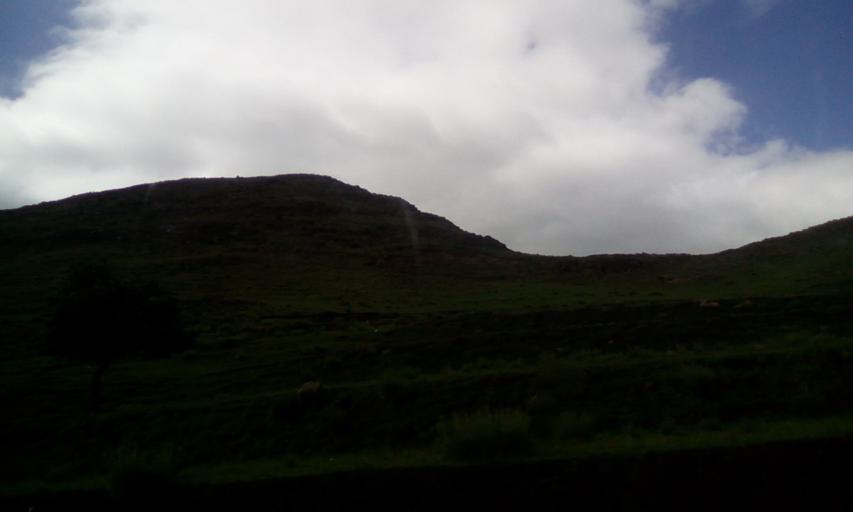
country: LS
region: Maseru
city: Nako
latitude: -29.6575
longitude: 27.8689
